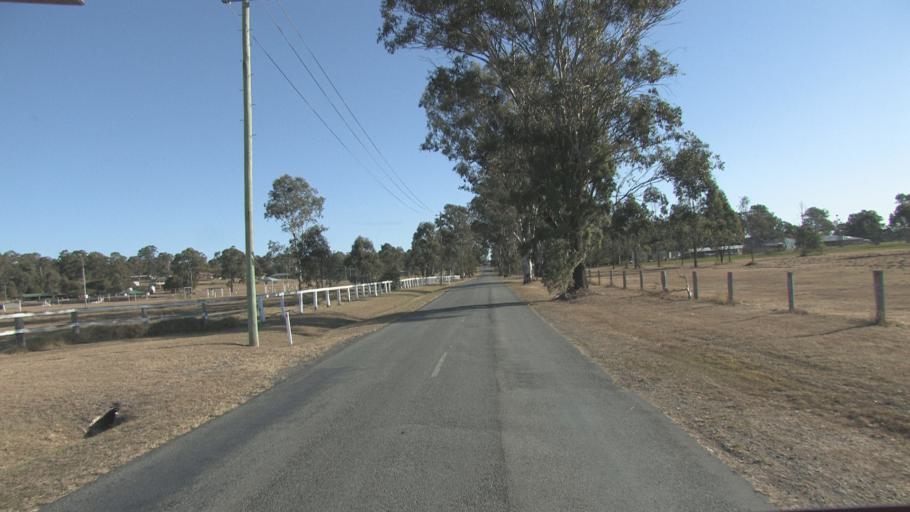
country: AU
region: Queensland
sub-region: Logan
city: North Maclean
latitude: -27.8295
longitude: 153.0115
